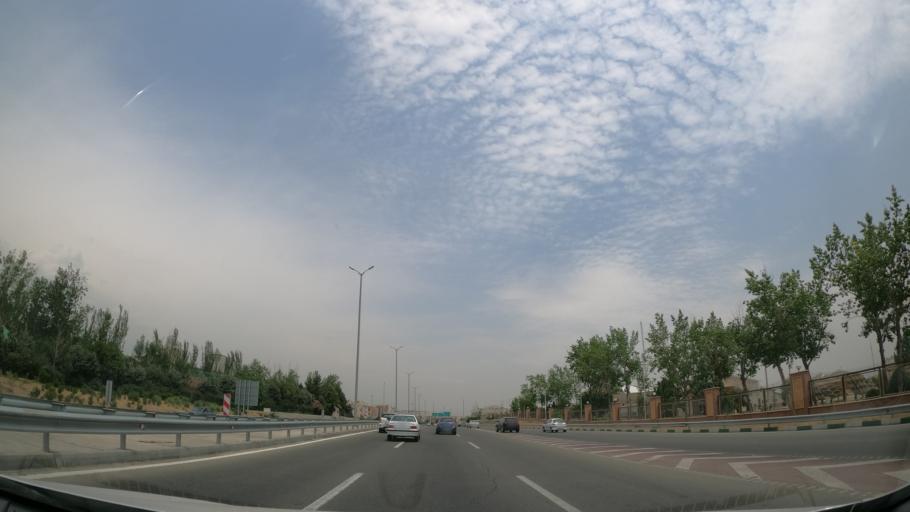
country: IR
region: Tehran
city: Shahr-e Qods
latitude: 35.7388
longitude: 51.2586
